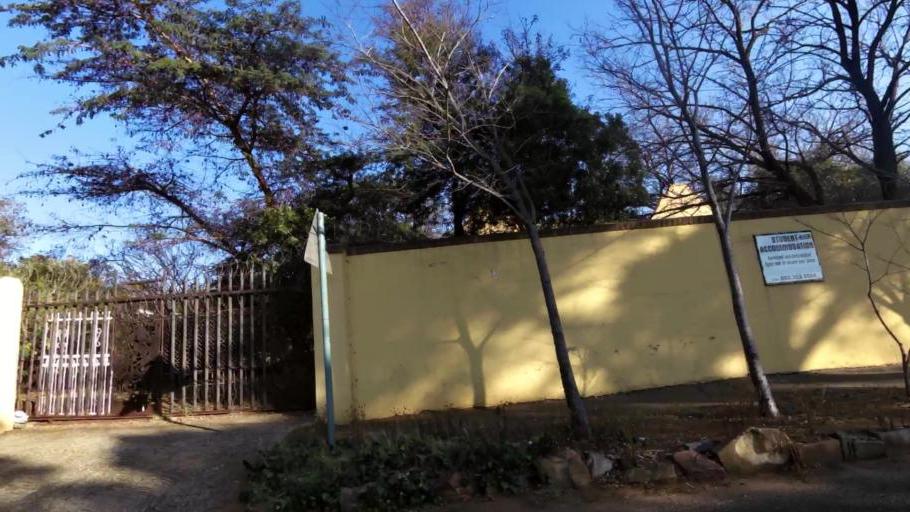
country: ZA
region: Gauteng
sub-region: City of Johannesburg Metropolitan Municipality
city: Johannesburg
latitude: -26.1891
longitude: 27.9937
